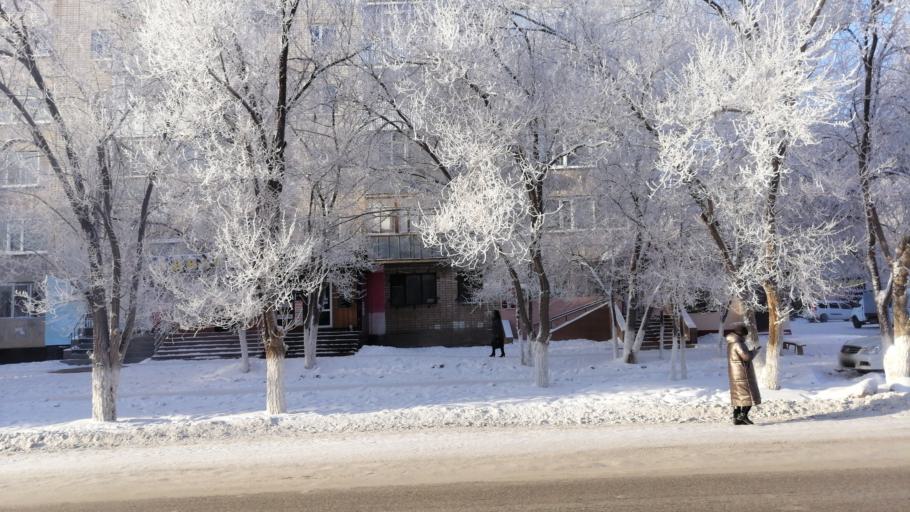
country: KZ
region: Aqtoebe
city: Aqtobe
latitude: 50.2927
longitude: 57.1494
